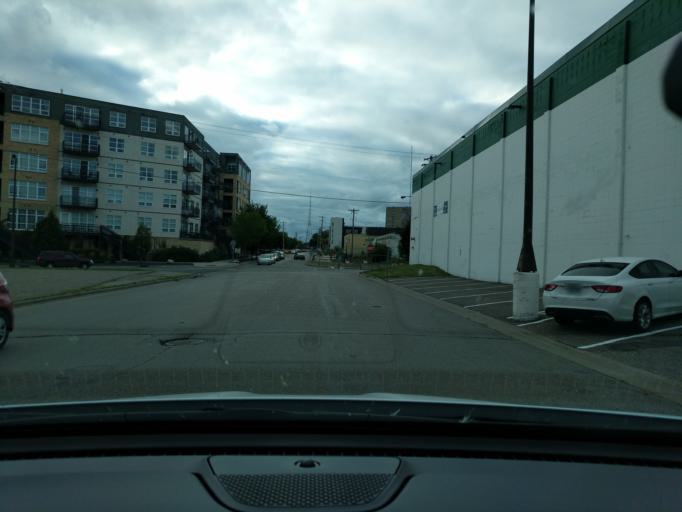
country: US
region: Minnesota
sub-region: Ramsey County
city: Falcon Heights
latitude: 44.9629
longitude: -93.1917
